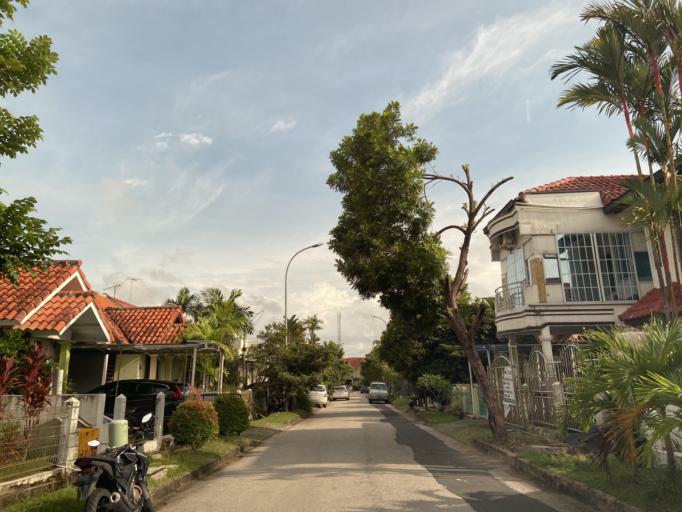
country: SG
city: Singapore
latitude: 1.1123
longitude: 104.0229
